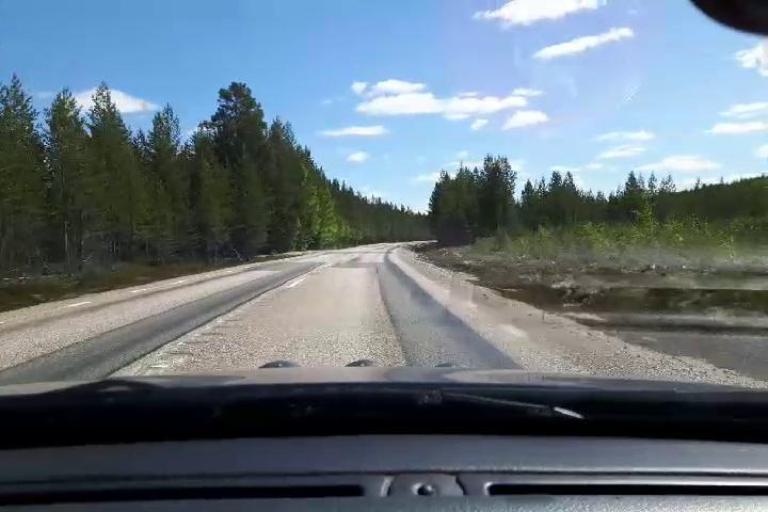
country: SE
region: Gaevleborg
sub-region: Ljusdals Kommun
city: Farila
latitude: 61.9722
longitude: 15.3444
